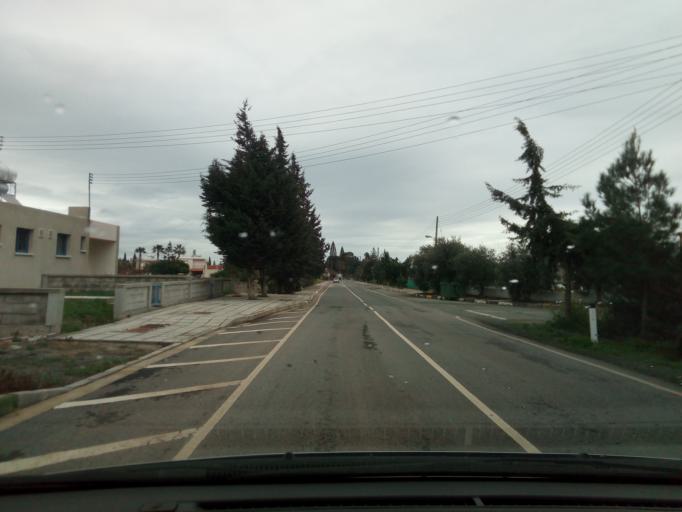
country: CY
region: Larnaka
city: Kofinou
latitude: 34.7275
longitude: 33.3318
